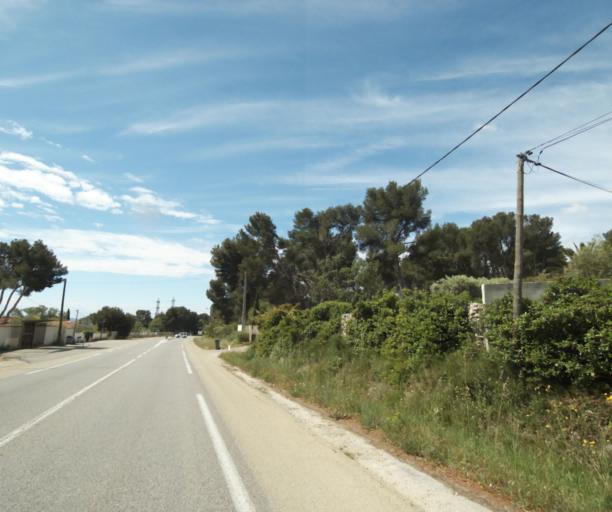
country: FR
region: Provence-Alpes-Cote d'Azur
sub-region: Departement des Bouches-du-Rhone
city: Rognac
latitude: 43.5103
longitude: 5.2257
